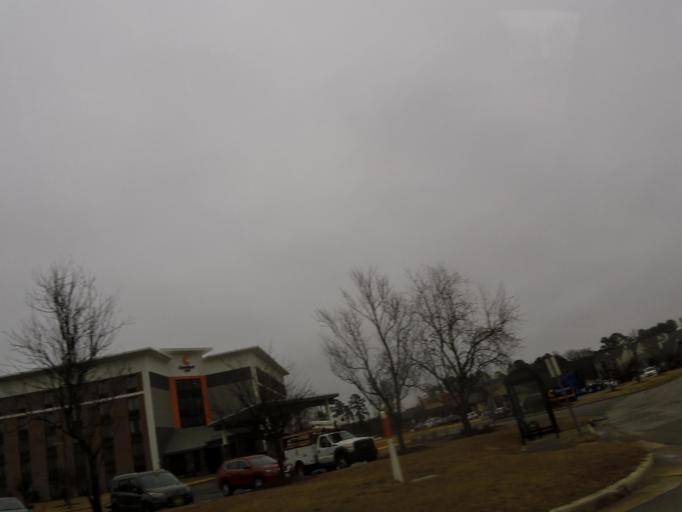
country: US
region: North Carolina
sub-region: Nash County
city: Rocky Mount
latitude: 35.9729
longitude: -77.8466
